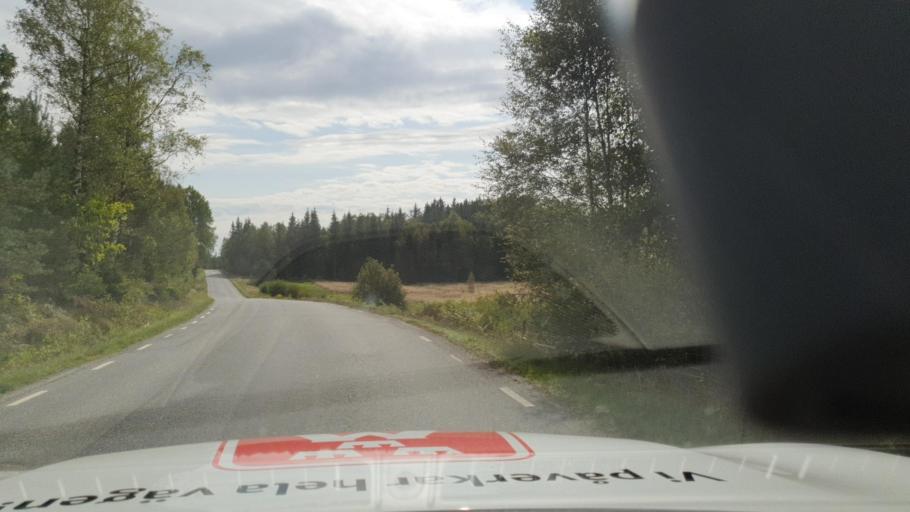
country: SE
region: Vaestra Goetaland
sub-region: Marks Kommun
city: Kinna
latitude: 57.3911
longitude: 12.7717
